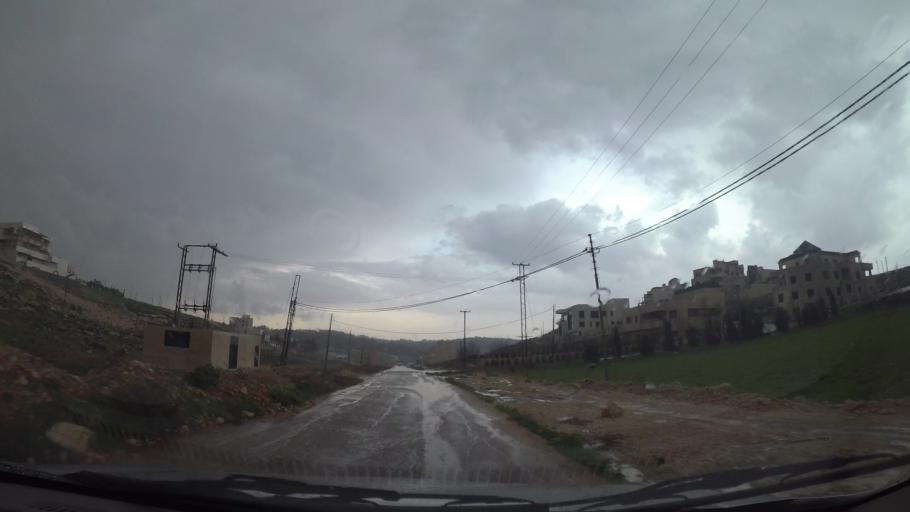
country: JO
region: Amman
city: Umm as Summaq
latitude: 31.8748
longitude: 35.8705
